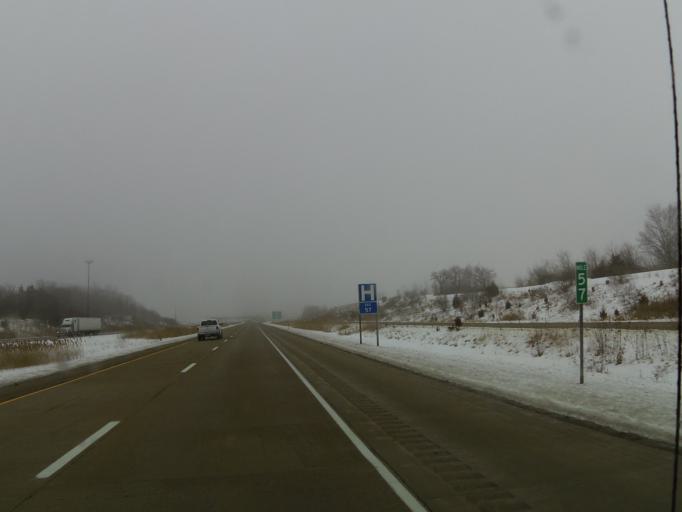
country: US
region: Illinois
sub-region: LaSalle County
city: La Salle
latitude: 41.3433
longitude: -89.0681
